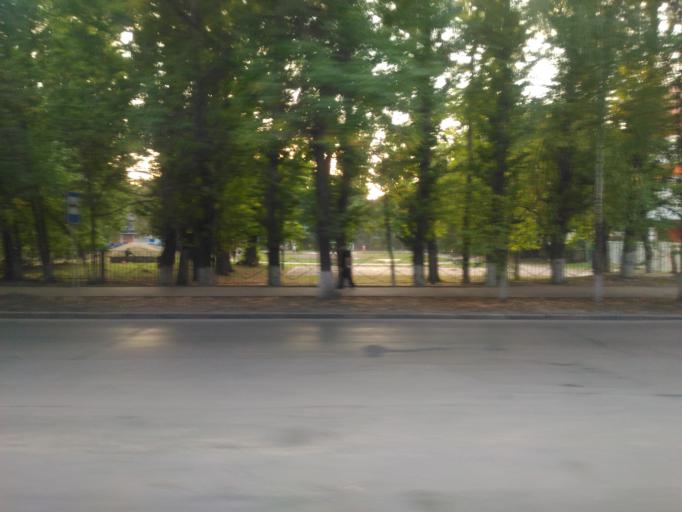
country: RU
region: Ulyanovsk
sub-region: Ulyanovskiy Rayon
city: Ulyanovsk
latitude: 54.3007
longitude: 48.3216
